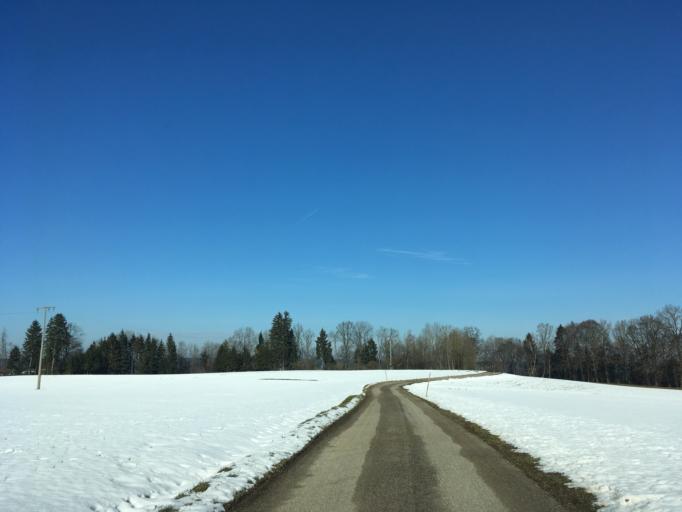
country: DE
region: Bavaria
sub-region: Upper Bavaria
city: Schechen
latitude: 47.9157
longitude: 12.1497
